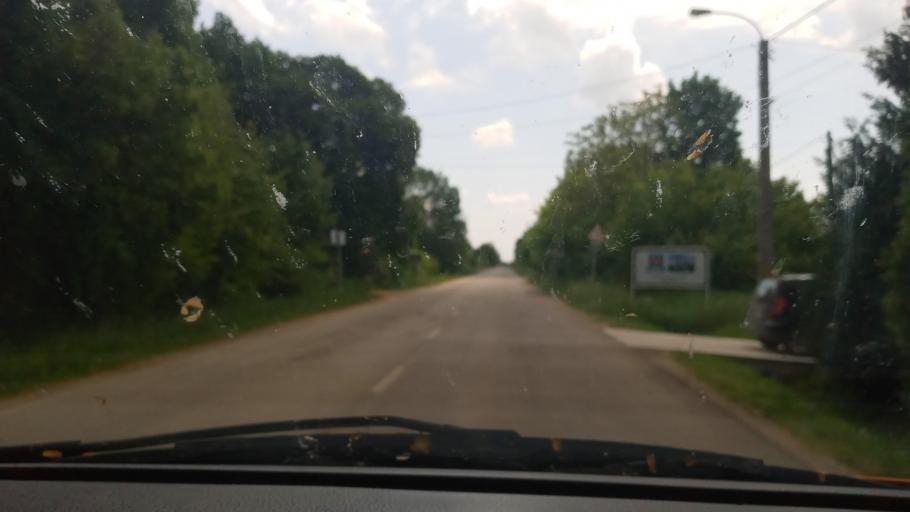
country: HU
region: Baranya
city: Beremend
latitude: 45.7765
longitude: 18.4425
